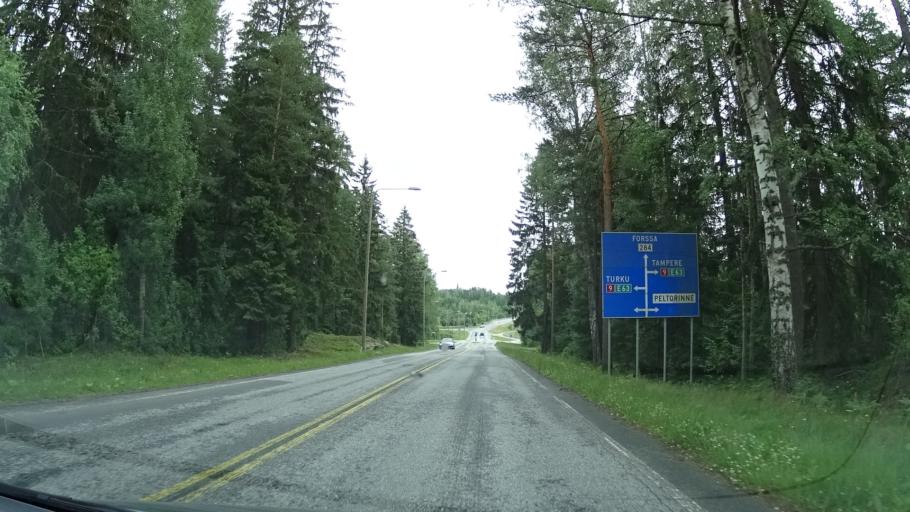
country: FI
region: Pirkanmaa
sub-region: Etelae-Pirkanmaa
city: Urjala
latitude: 61.0827
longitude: 23.5282
